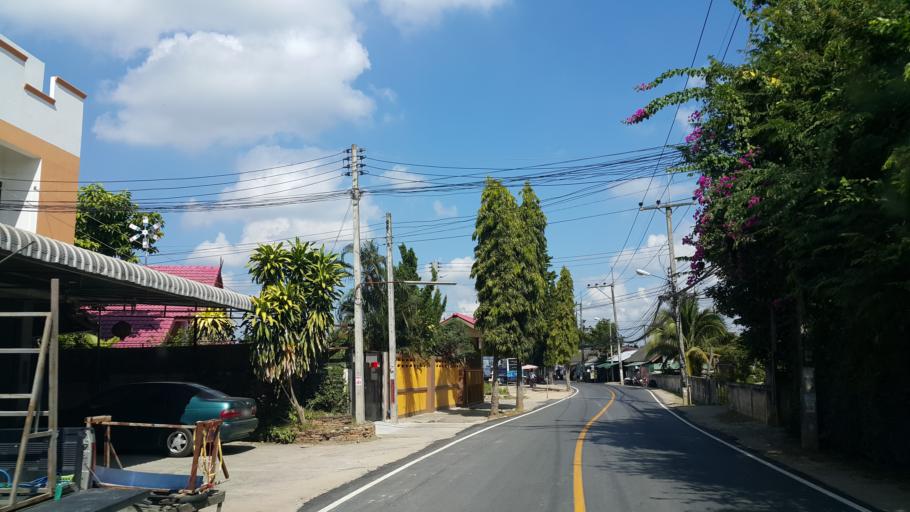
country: TH
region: Chiang Mai
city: San Sai
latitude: 18.8421
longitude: 99.0180
